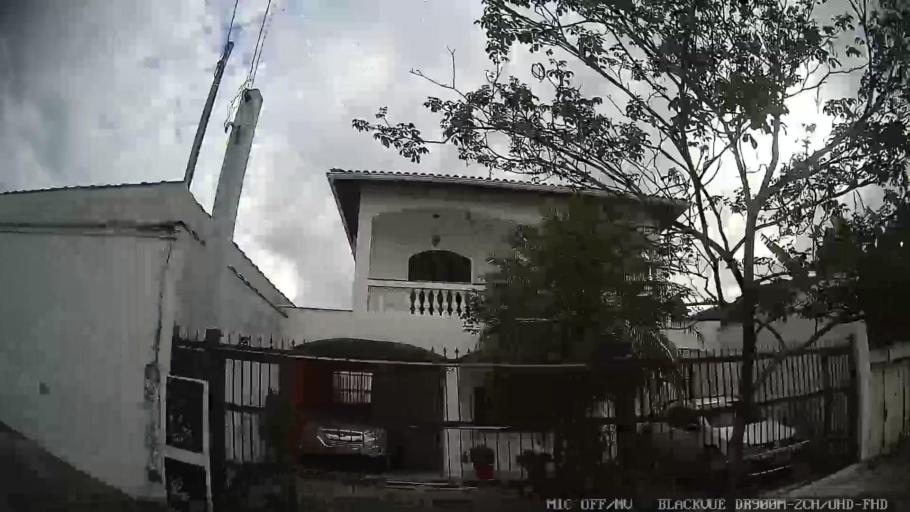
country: BR
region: Sao Paulo
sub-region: Guaruja
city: Guaruja
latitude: -23.9798
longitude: -46.2343
